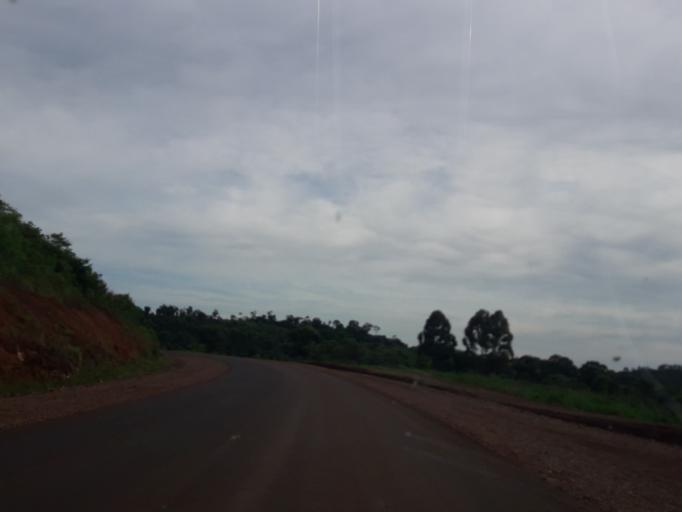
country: AR
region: Misiones
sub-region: Departamento de San Pedro
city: San Pedro
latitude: -26.5312
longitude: -53.9397
